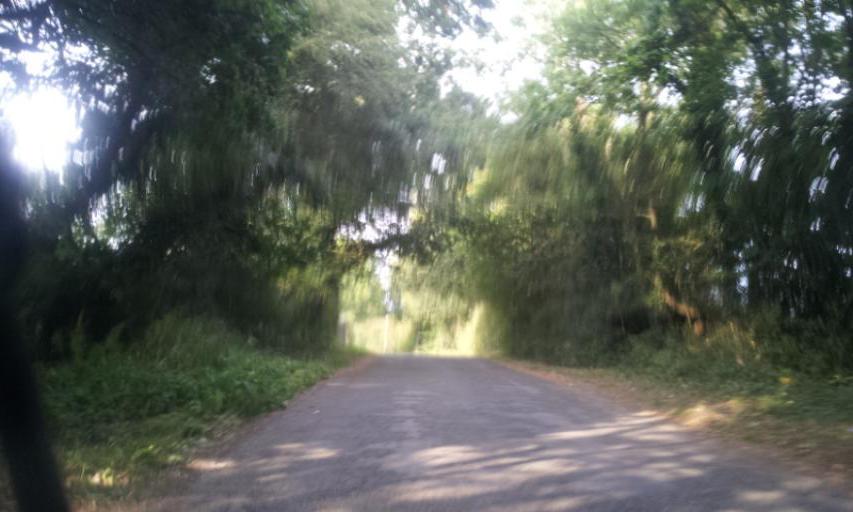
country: GB
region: England
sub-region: Kent
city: Yalding
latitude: 51.1993
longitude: 0.4158
